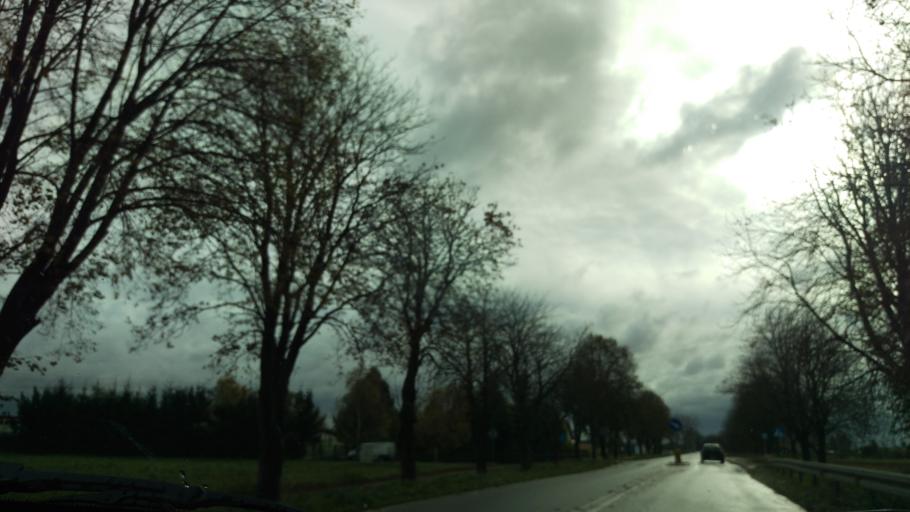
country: PL
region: West Pomeranian Voivodeship
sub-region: Powiat gryficki
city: Ploty
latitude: 53.8209
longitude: 15.2524
